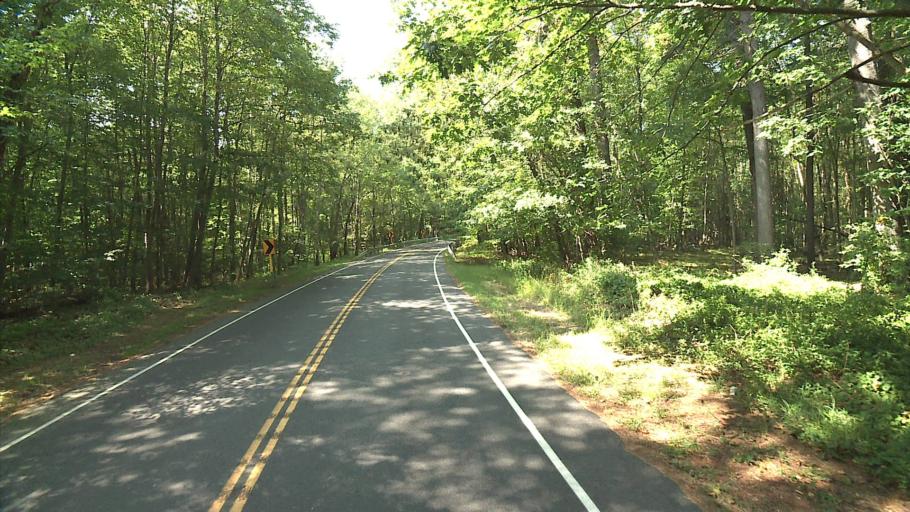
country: US
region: Connecticut
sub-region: Fairfield County
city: Southport
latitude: 41.2200
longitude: -73.3092
